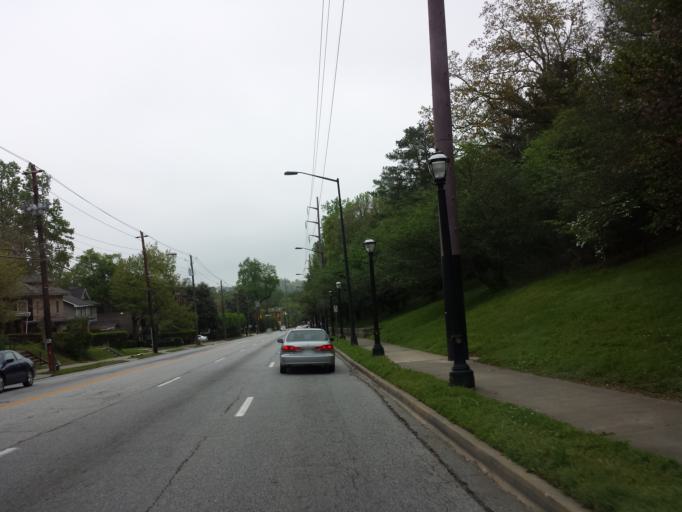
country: US
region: Georgia
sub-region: DeKalb County
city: Druid Hills
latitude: 33.7902
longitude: -84.3754
